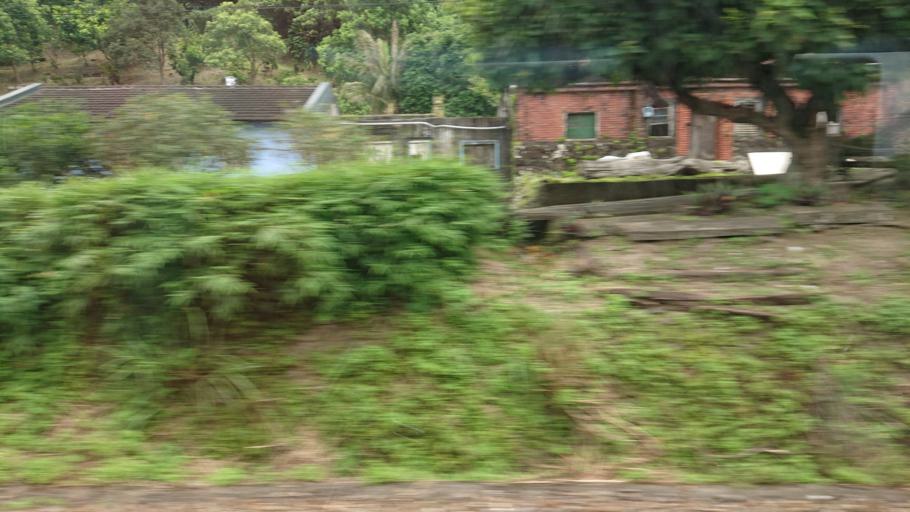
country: TW
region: Taiwan
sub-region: Keelung
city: Keelung
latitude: 24.9524
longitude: 121.9124
